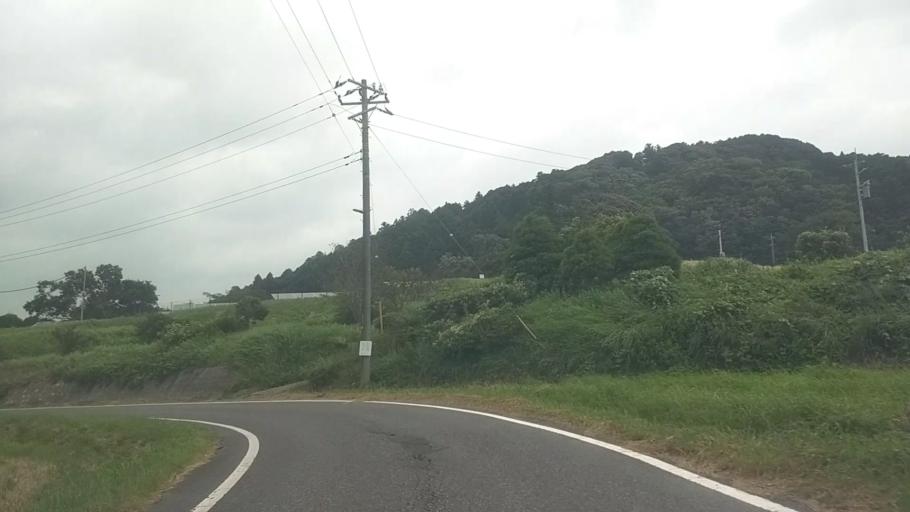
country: JP
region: Chiba
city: Kawaguchi
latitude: 35.2605
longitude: 140.0579
